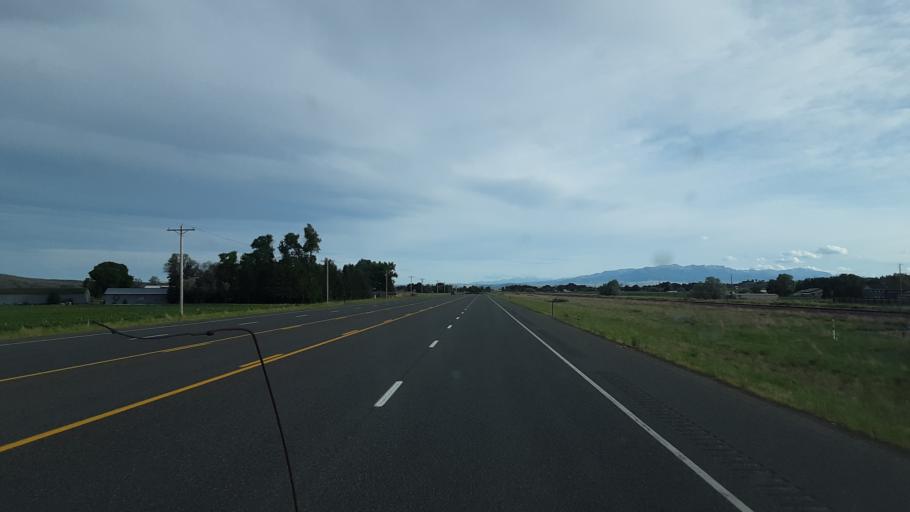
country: US
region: Wyoming
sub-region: Park County
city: Cody
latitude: 44.6113
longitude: -108.9611
